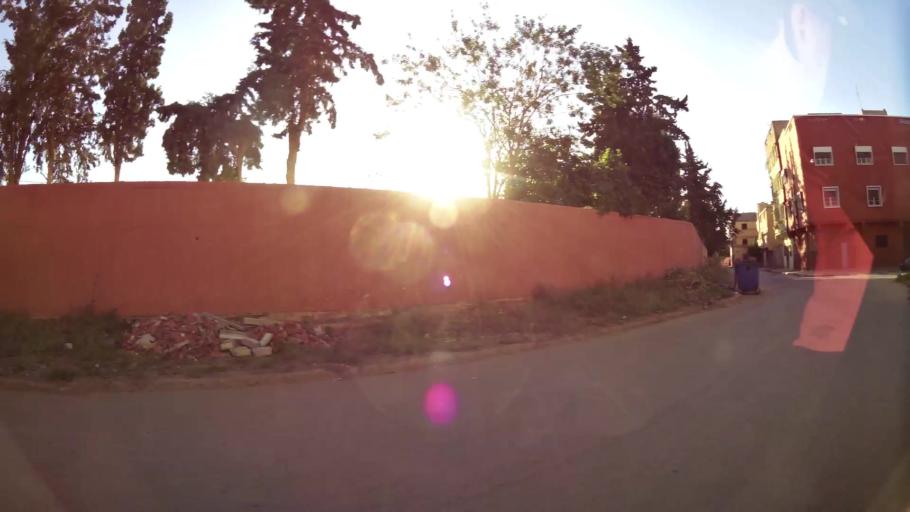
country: MA
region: Oriental
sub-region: Berkane-Taourirt
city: Berkane
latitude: 34.9297
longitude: -2.3263
